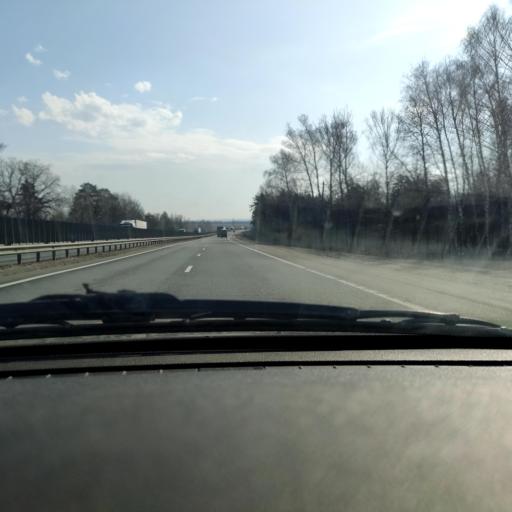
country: RU
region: Samara
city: Bogatyr'
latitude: 53.5113
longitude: 49.9421
